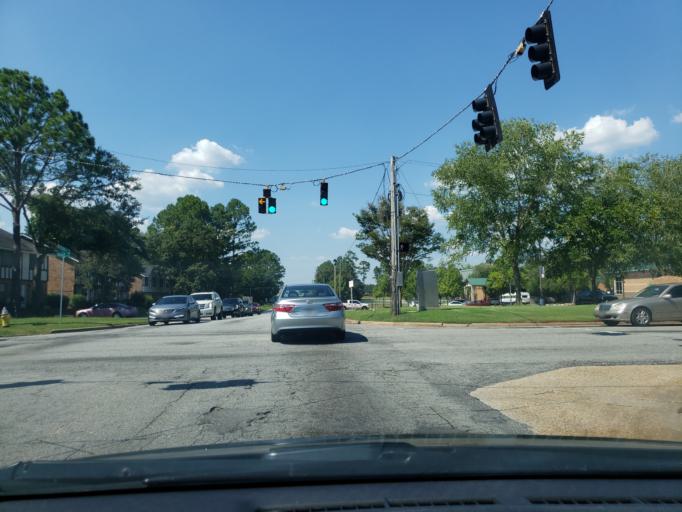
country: US
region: Georgia
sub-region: Dougherty County
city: Albany
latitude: 31.6118
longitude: -84.2042
